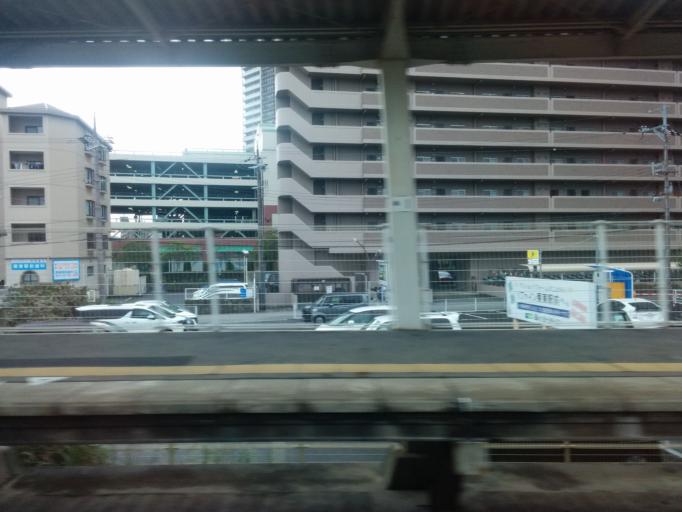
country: JP
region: Shiga Prefecture
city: Kusatsu
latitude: 35.0381
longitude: 135.9809
